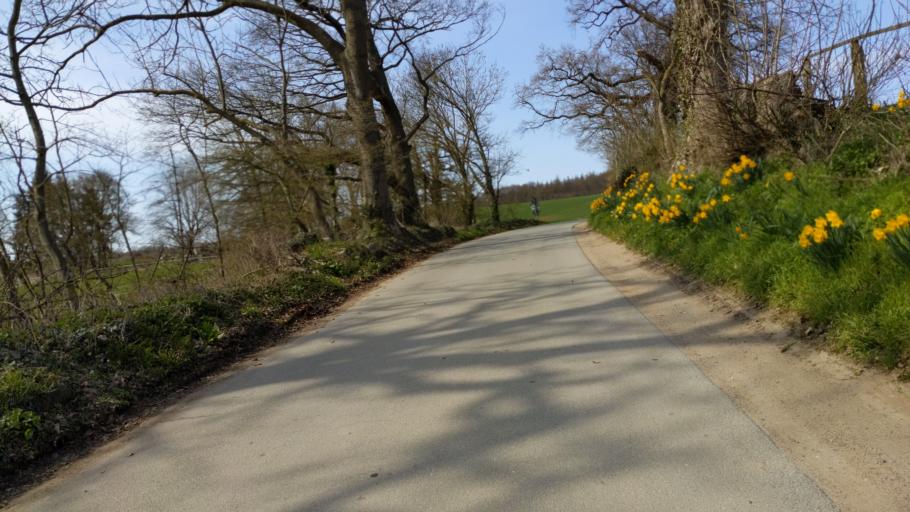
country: DE
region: Schleswig-Holstein
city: Schashagen
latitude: 54.1154
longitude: 10.8948
